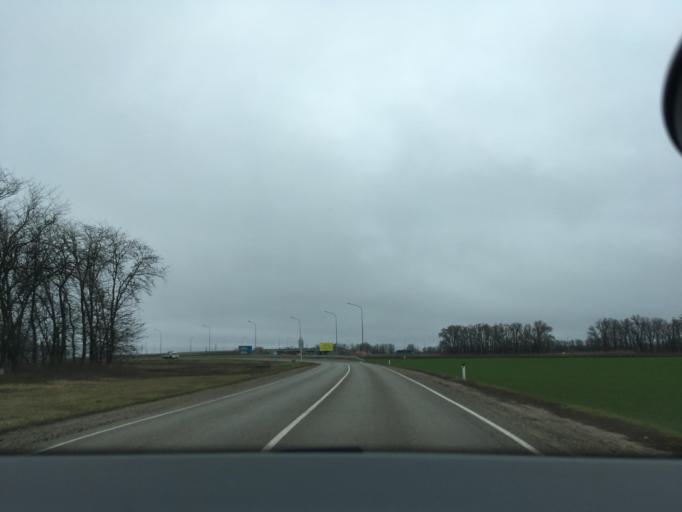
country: RU
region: Krasnodarskiy
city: Kushchevskaya
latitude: 46.6027
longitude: 39.6576
